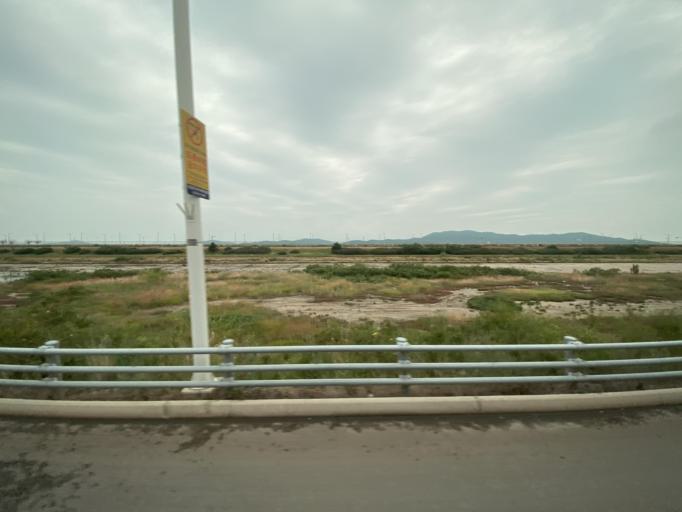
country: KR
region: Incheon
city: Seonwon
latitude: 37.4960
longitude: 126.4323
